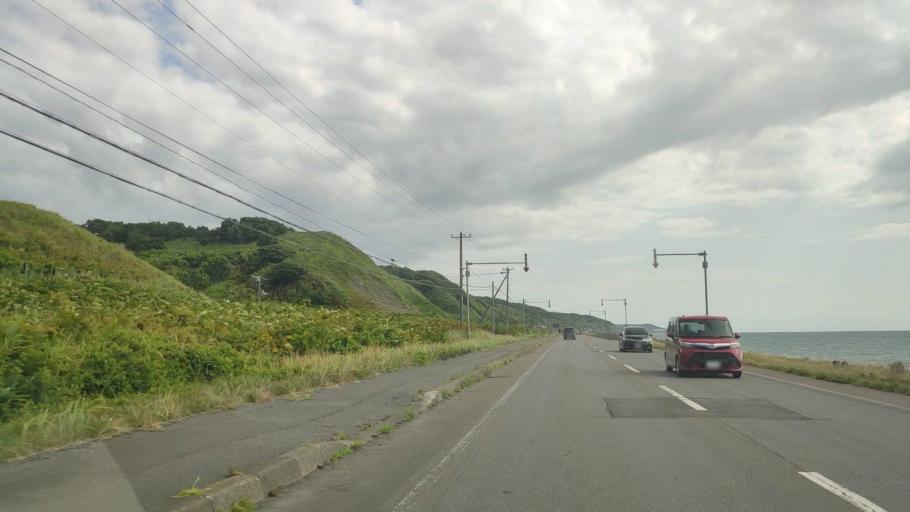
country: JP
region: Hokkaido
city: Rumoi
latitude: 44.1956
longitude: 141.6579
